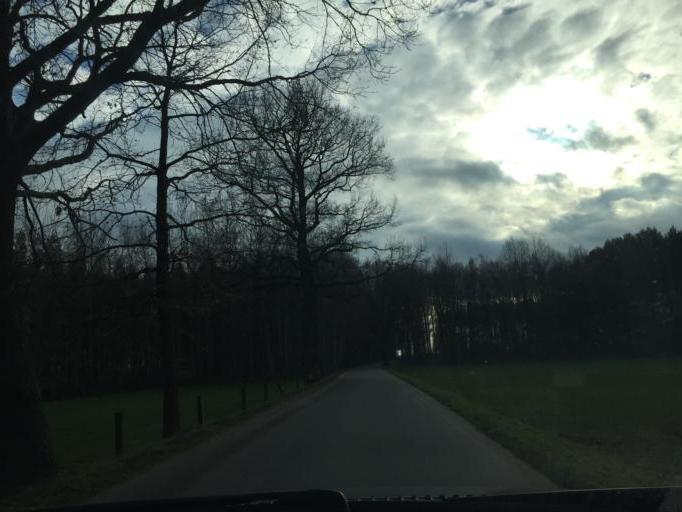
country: DE
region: Saxony
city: Ebersbach
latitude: 51.2108
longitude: 13.6723
